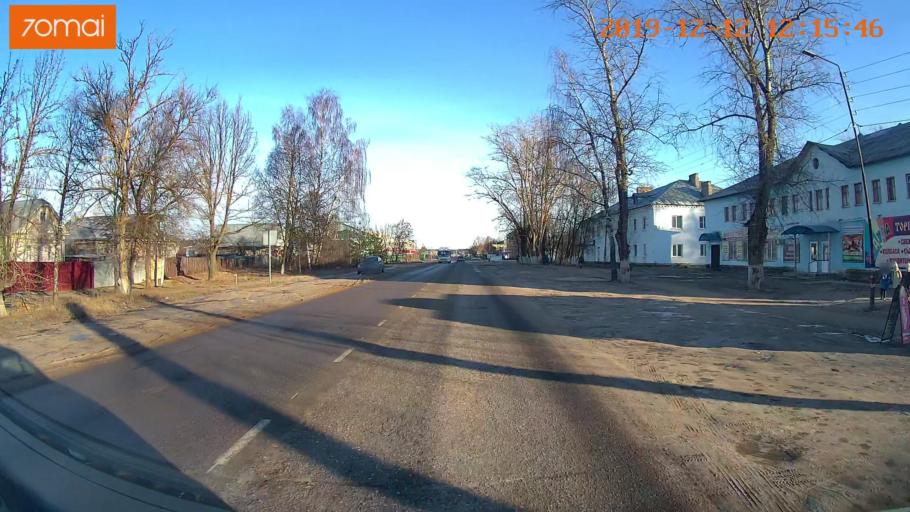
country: RU
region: Ivanovo
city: Kokhma
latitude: 56.9379
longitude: 41.1022
